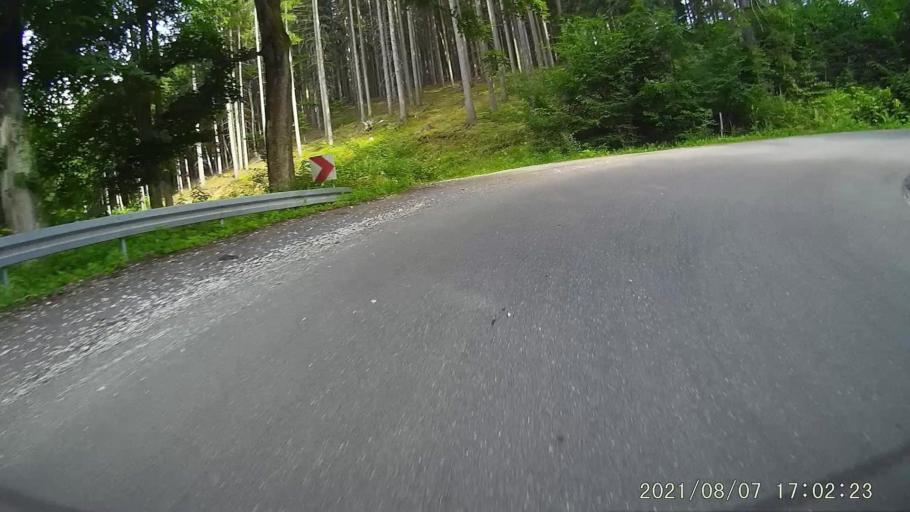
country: PL
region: Lower Silesian Voivodeship
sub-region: Powiat klodzki
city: Bystrzyca Klodzka
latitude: 50.2872
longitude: 16.5620
